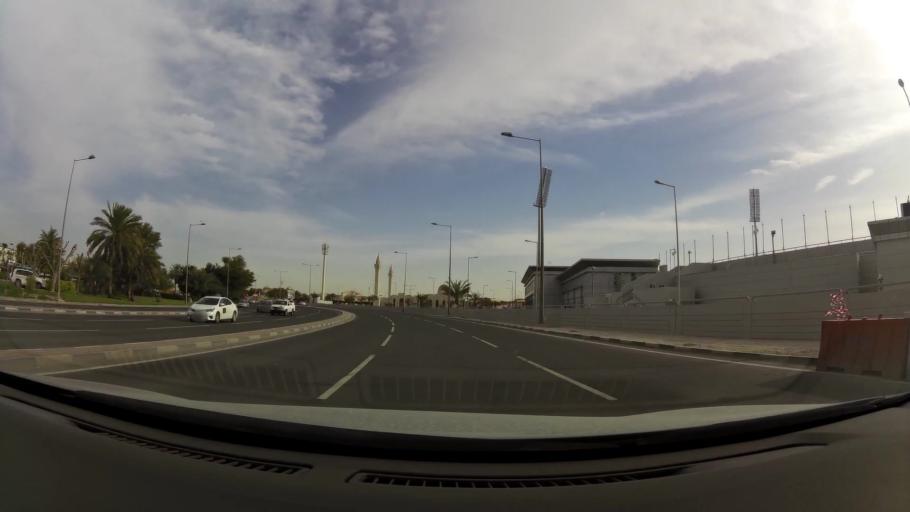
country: QA
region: Baladiyat ad Dawhah
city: Doha
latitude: 25.2529
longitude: 51.5363
